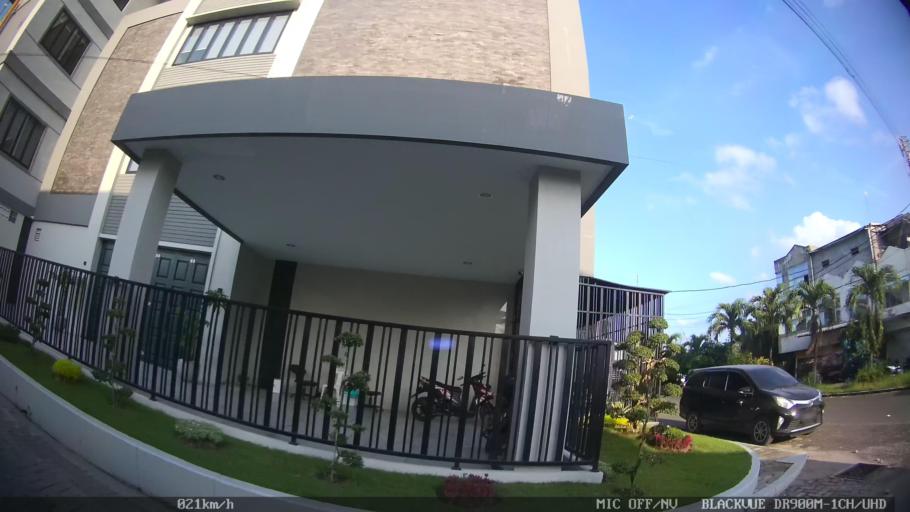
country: ID
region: North Sumatra
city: Medan
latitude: 3.6197
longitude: 98.6550
